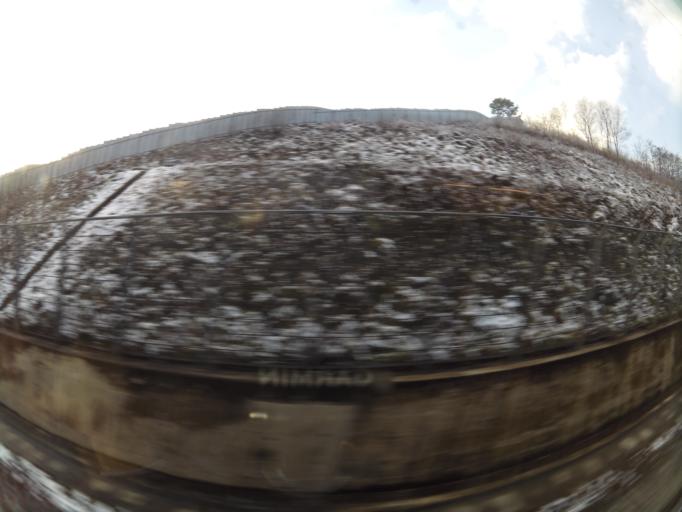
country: KR
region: Daejeon
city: Songgang-dong
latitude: 36.4230
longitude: 127.4160
